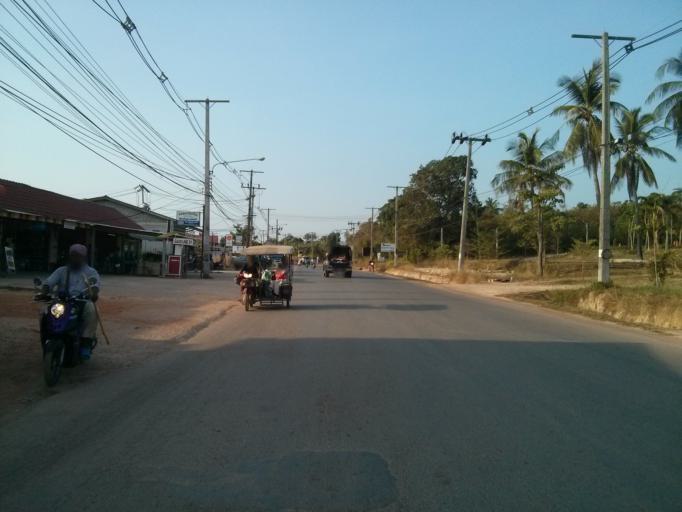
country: TH
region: Krabi
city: Saladan
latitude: 7.5915
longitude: 99.0356
